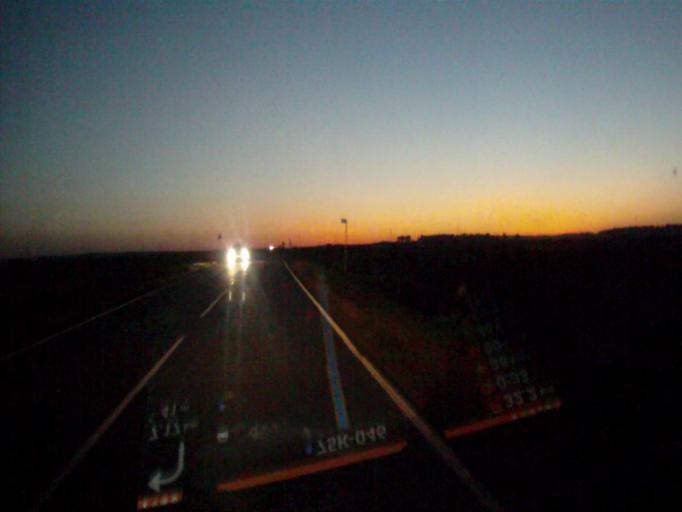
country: RU
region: Chelyabinsk
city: Chebarkul'
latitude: 55.2205
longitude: 60.5613
